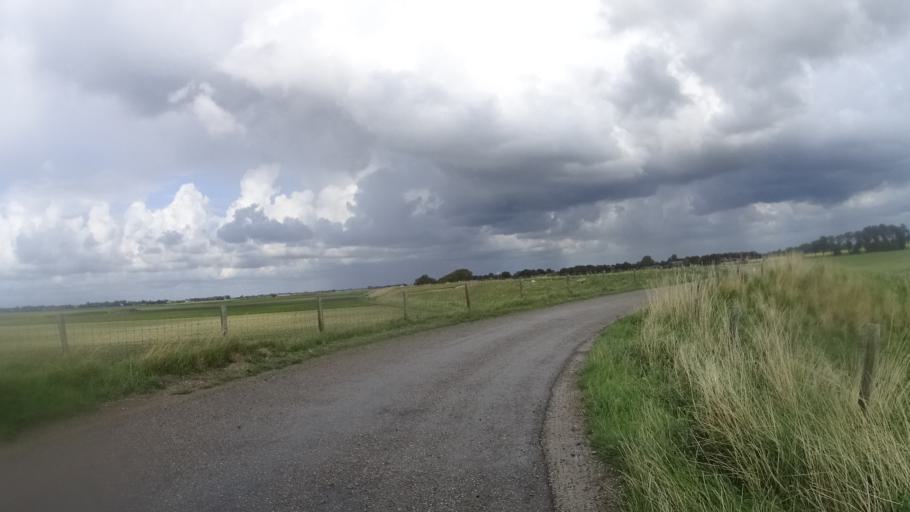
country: NL
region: North Holland
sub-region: Gemeente Schagen
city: Harenkarspel
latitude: 52.7660
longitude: 4.7308
